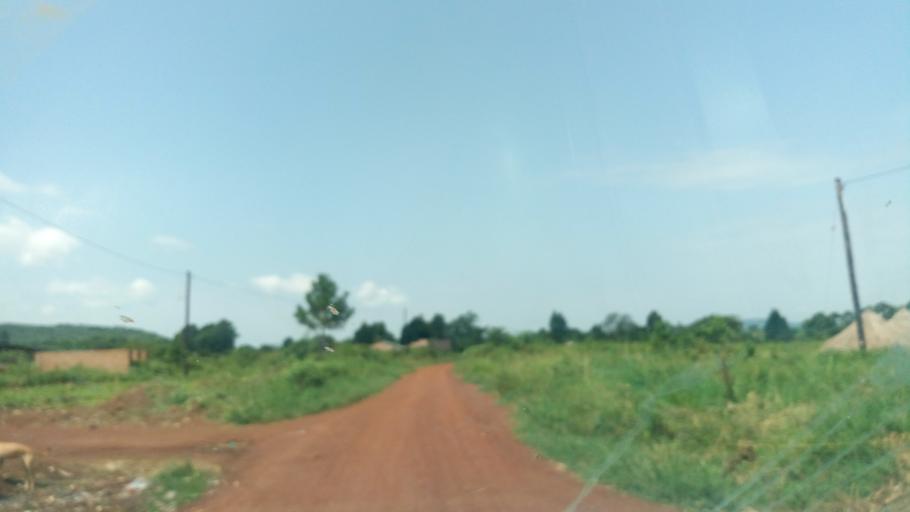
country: UG
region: Western Region
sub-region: Masindi District
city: Masindi
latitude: 1.6854
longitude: 31.8353
